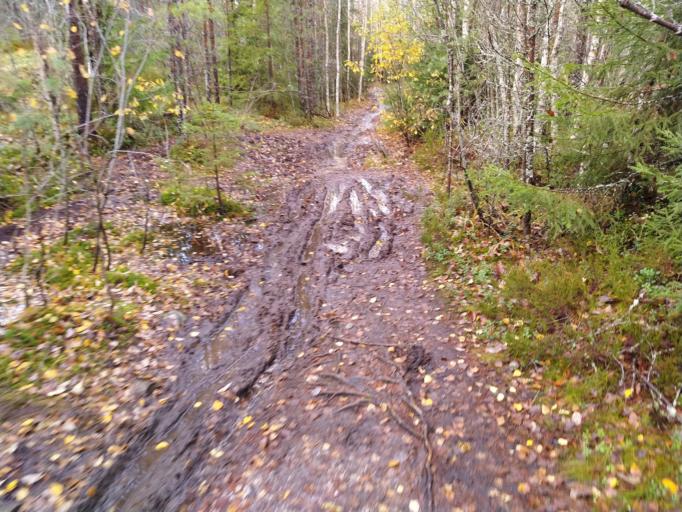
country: FI
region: Uusimaa
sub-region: Helsinki
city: Sibbo
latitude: 60.3056
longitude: 25.2151
